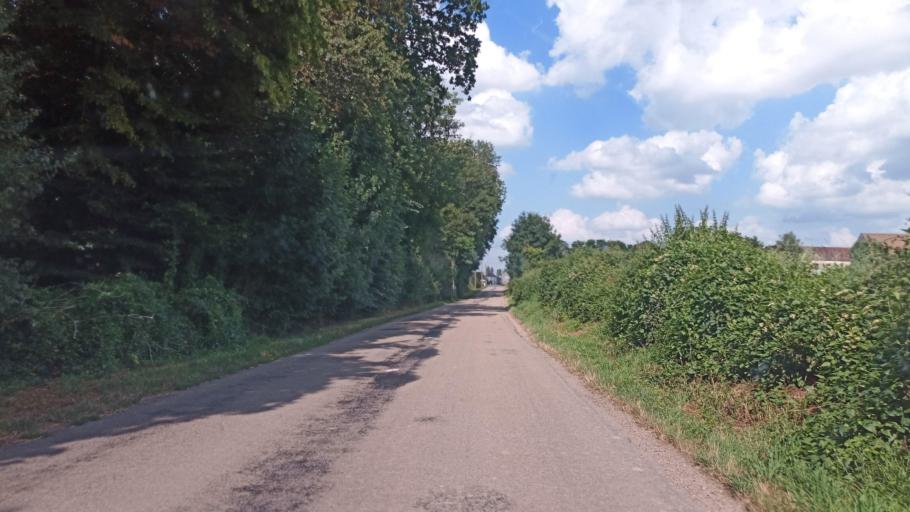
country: FR
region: Bourgogne
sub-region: Departement de l'Yonne
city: Egriselles-le-Bocage
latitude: 48.0200
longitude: 3.1706
